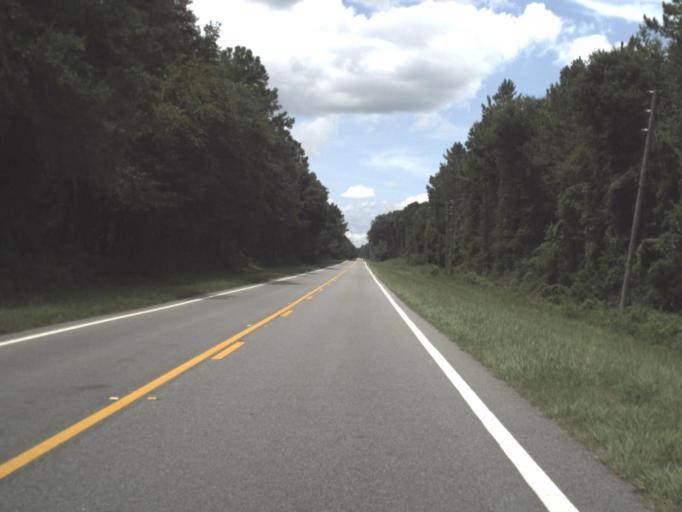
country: US
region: Florida
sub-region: Madison County
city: Madison
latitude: 30.5767
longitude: -83.3565
